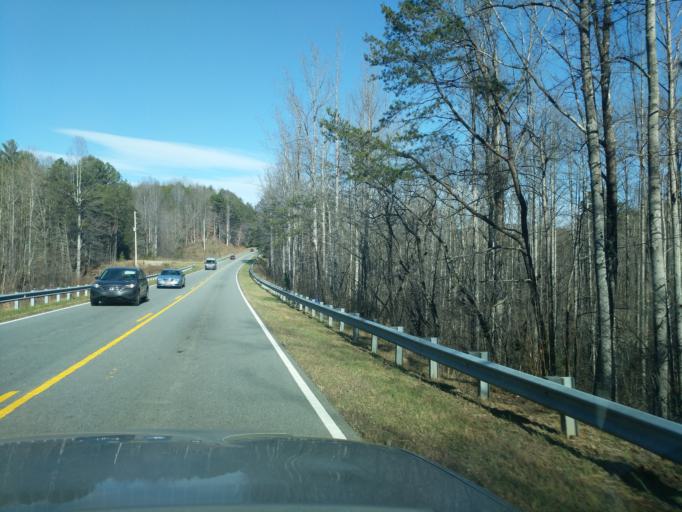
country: US
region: North Carolina
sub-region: McDowell County
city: West Marion
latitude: 35.5371
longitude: -81.9659
